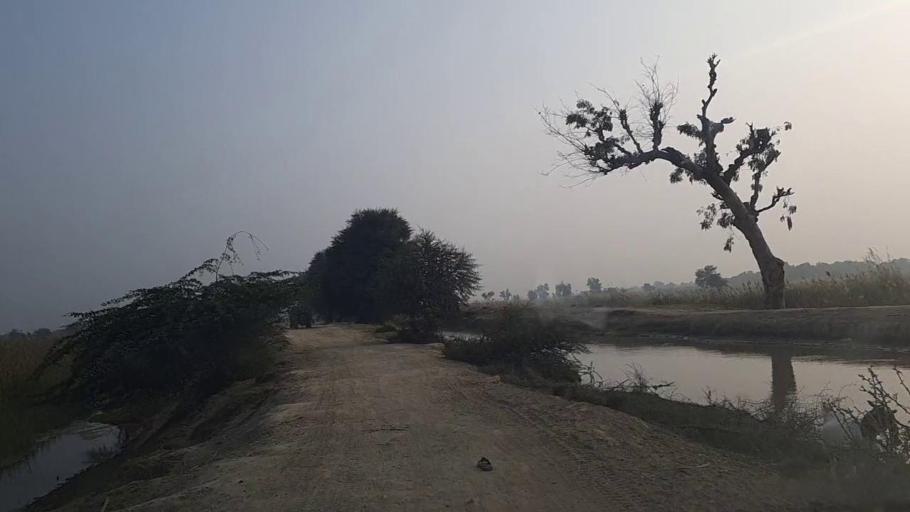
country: PK
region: Sindh
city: Khadro
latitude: 26.1263
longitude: 68.7998
